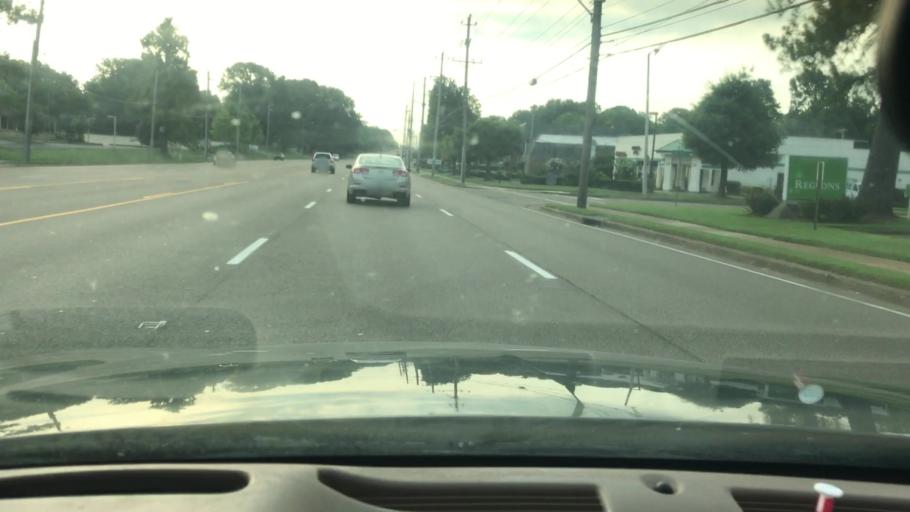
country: US
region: Tennessee
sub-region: Shelby County
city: Bartlett
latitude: 35.2046
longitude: -89.8557
